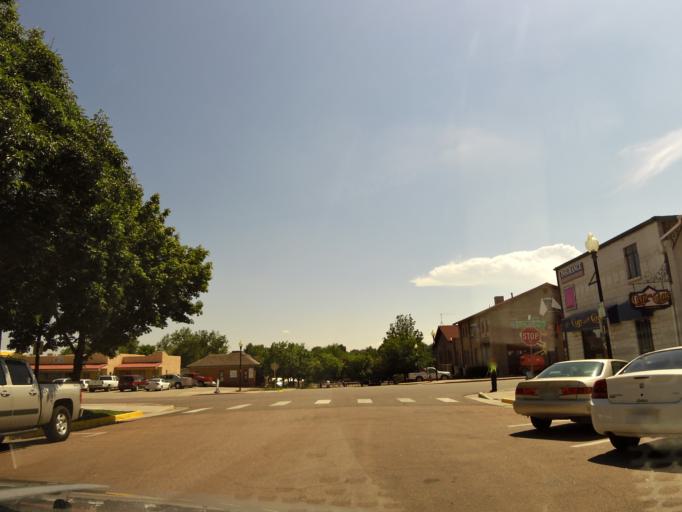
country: US
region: Colorado
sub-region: Fremont County
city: Canon City
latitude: 38.4394
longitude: -105.2416
